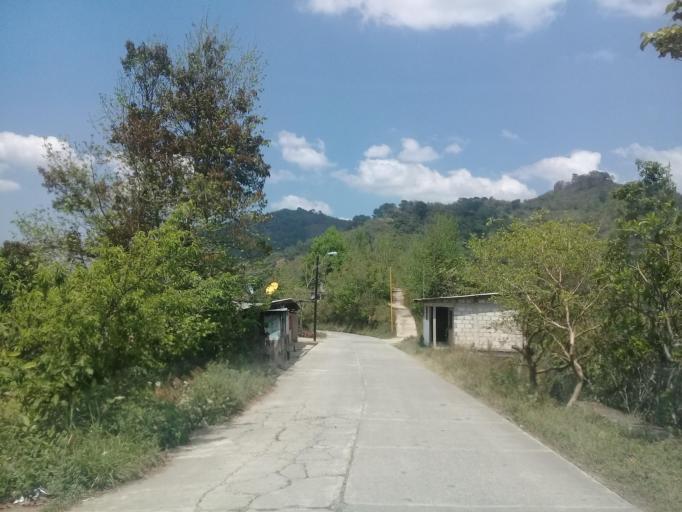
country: MX
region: Veracruz
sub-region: Tlilapan
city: Tonalixco
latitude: 18.7938
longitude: -97.0560
